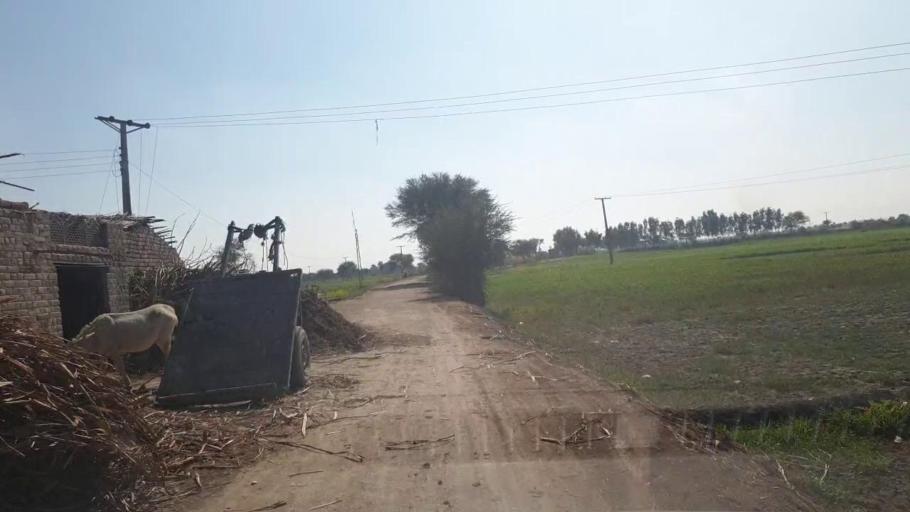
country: PK
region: Sindh
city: Shahdadpur
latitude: 25.9190
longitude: 68.5836
